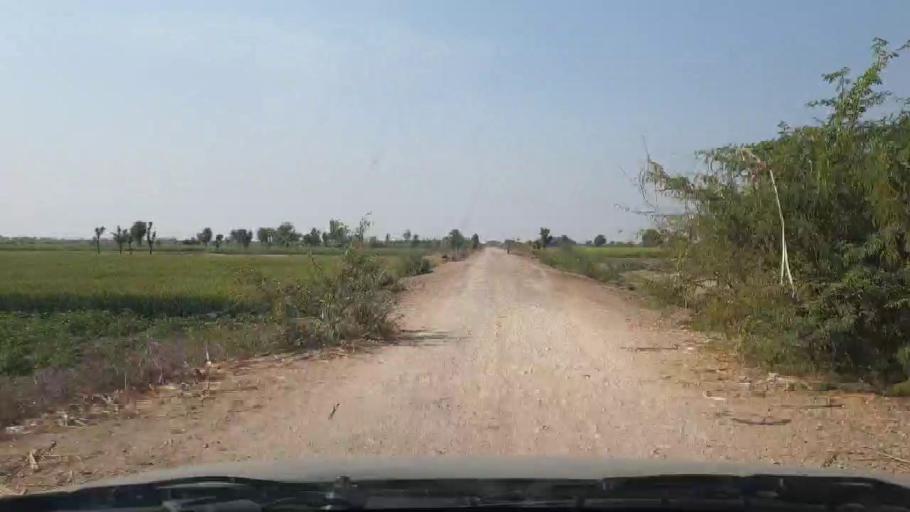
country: PK
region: Sindh
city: Samaro
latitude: 25.1919
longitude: 69.3498
